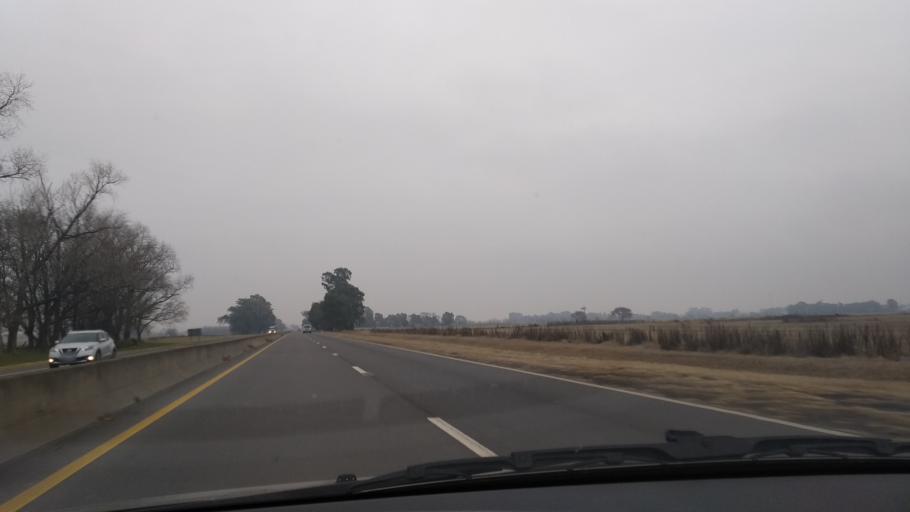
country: AR
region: Buenos Aires
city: Olavarria
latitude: -36.8670
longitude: -60.1295
